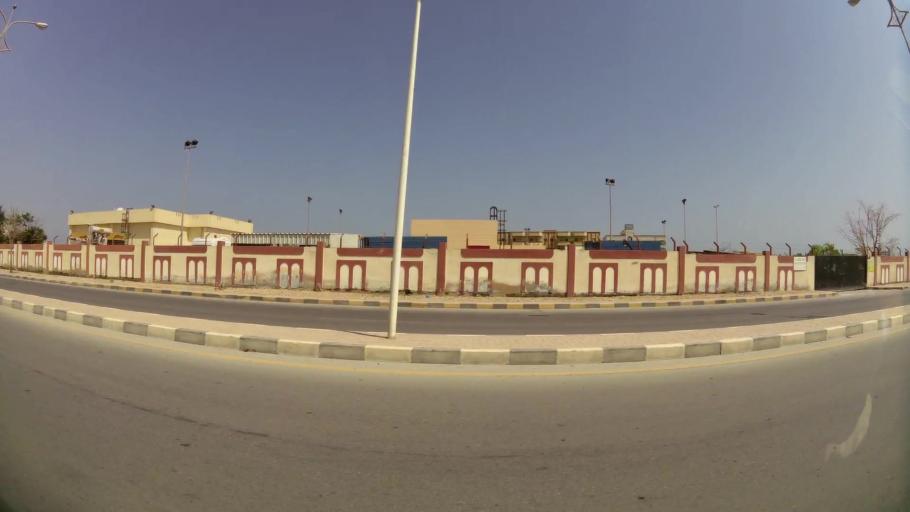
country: OM
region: Zufar
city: Salalah
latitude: 17.0097
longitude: 54.0752
